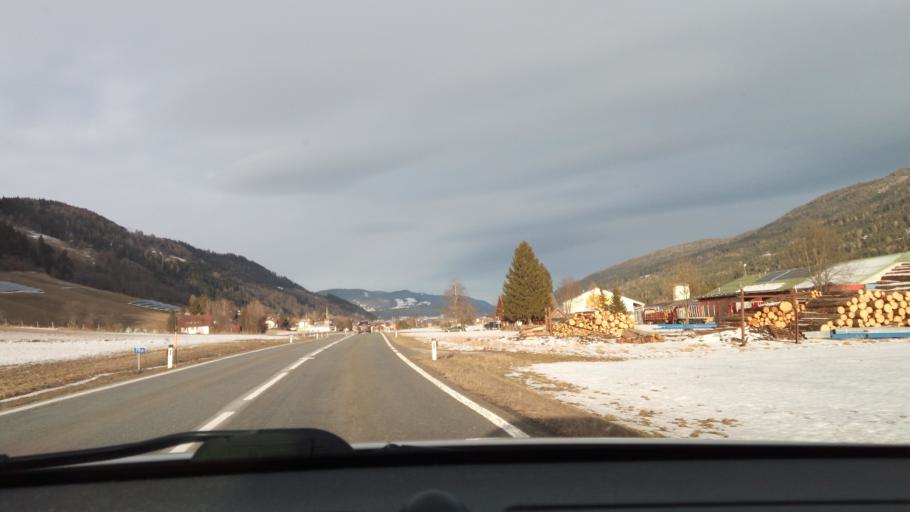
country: AT
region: Salzburg
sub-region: Politischer Bezirk Tamsweg
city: Mariapfarr
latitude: 47.1084
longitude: 13.7287
